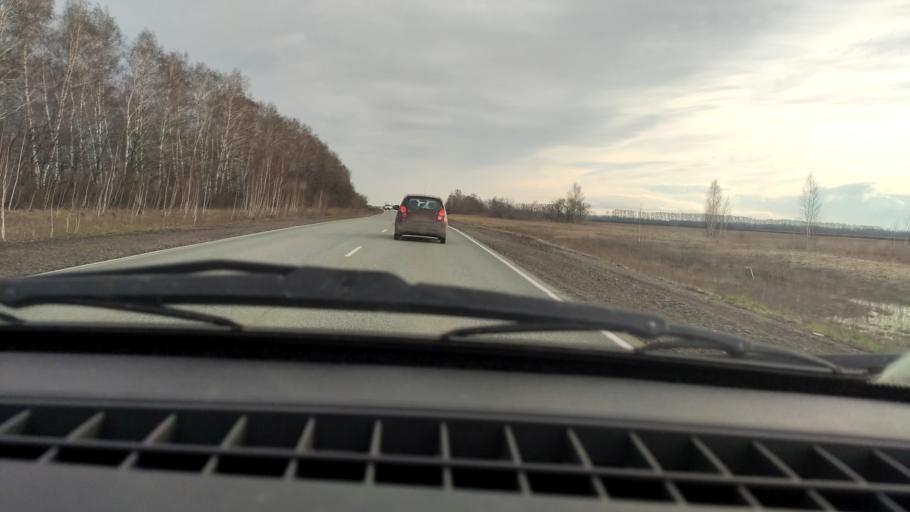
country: RU
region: Bashkortostan
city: Chishmy
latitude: 54.4160
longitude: 55.2250
